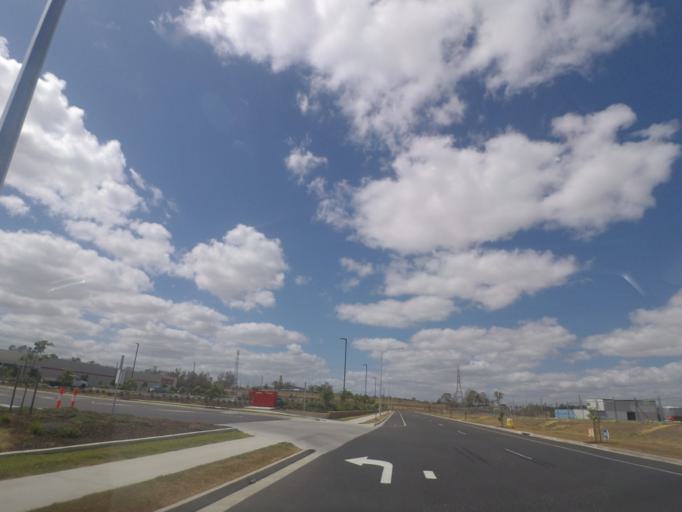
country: AU
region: Queensland
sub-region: Ipswich
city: Bundamba
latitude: -27.5894
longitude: 152.8204
